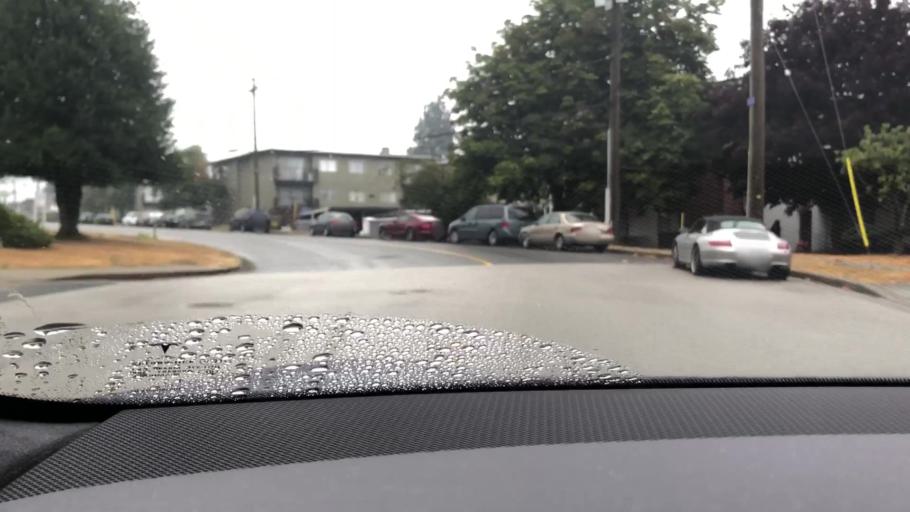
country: CA
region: British Columbia
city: New Westminster
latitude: 49.2198
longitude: -122.9533
